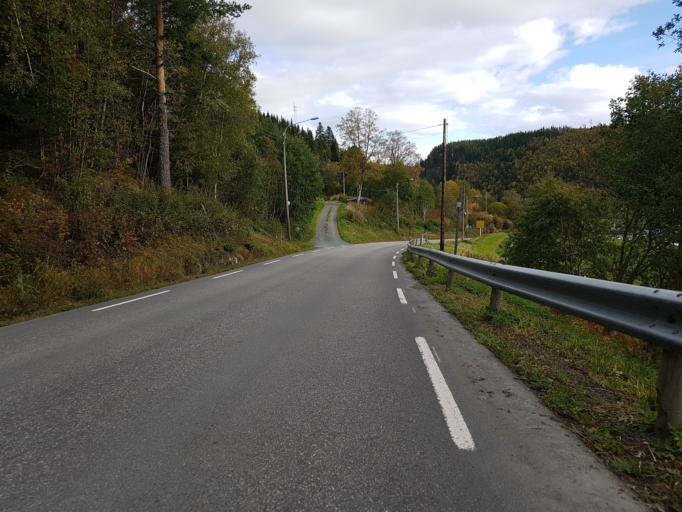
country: NO
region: Sor-Trondelag
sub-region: Klaebu
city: Klaebu
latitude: 63.3974
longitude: 10.5418
